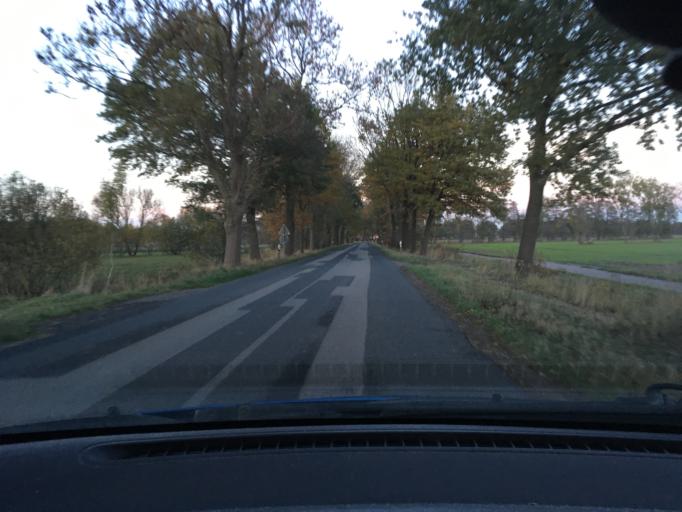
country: DE
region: Lower Saxony
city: Radbruch
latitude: 53.3302
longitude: 10.2989
